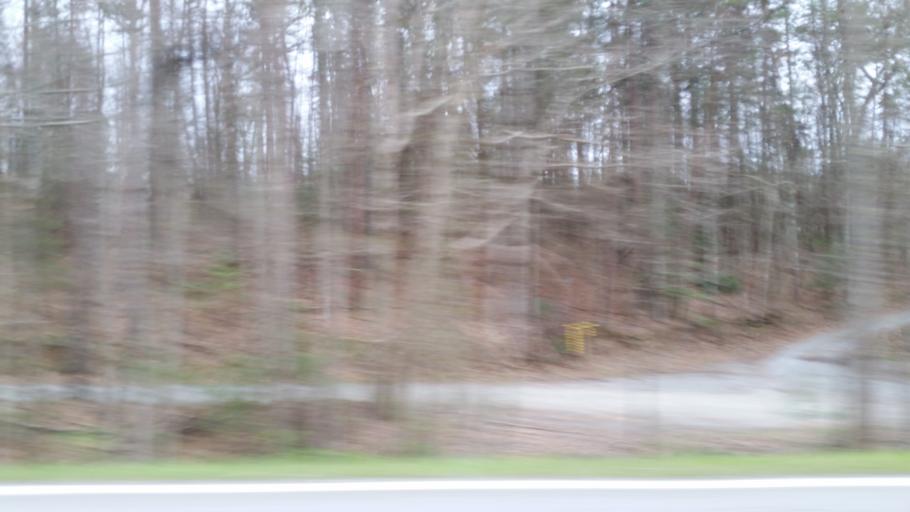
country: US
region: Georgia
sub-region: Fannin County
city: Blue Ridge
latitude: 34.8007
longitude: -84.2778
